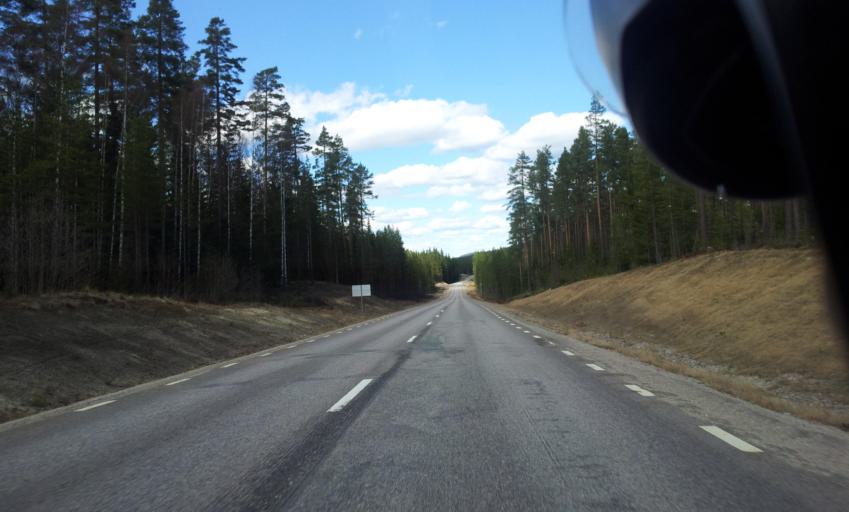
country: SE
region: Gaevleborg
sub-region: Bollnas Kommun
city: Vittsjo
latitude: 61.1611
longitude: 15.8818
